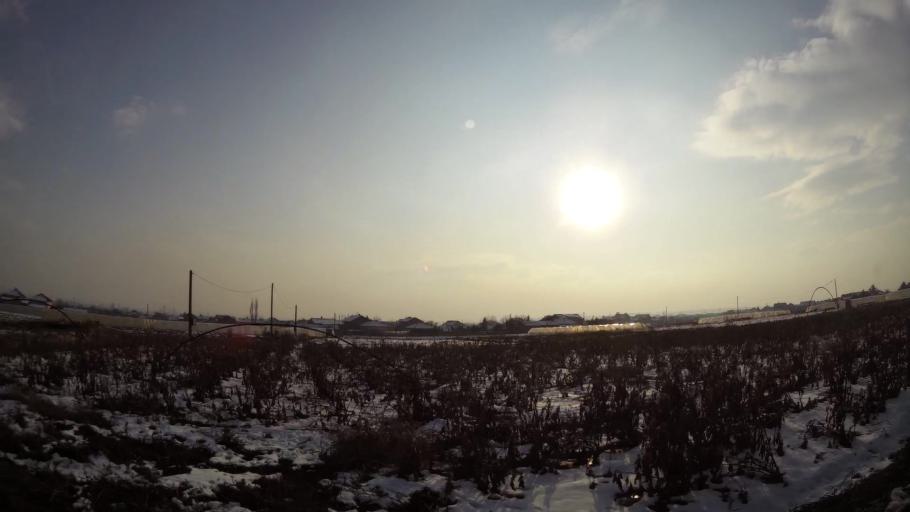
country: MK
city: Creshevo
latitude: 42.0330
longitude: 21.5240
